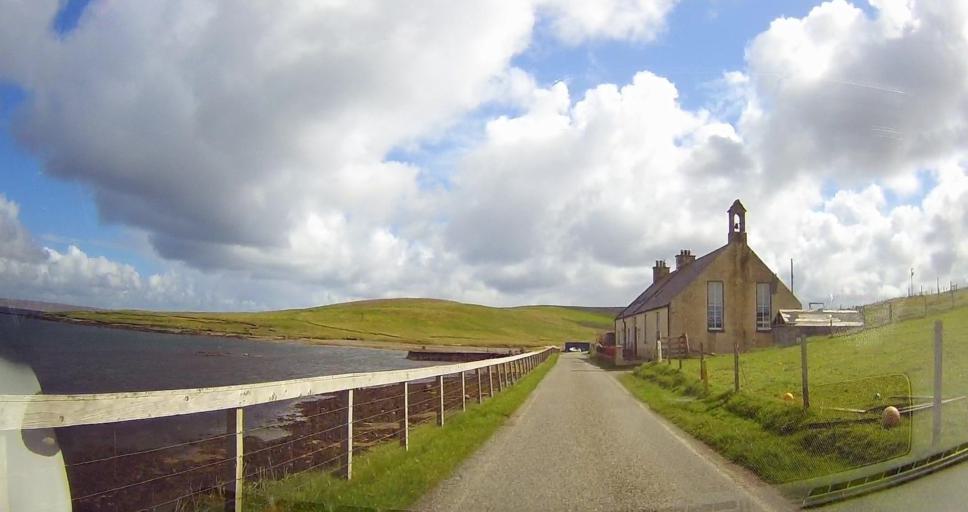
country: GB
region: Scotland
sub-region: Shetland Islands
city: Lerwick
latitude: 60.5789
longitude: -1.3325
